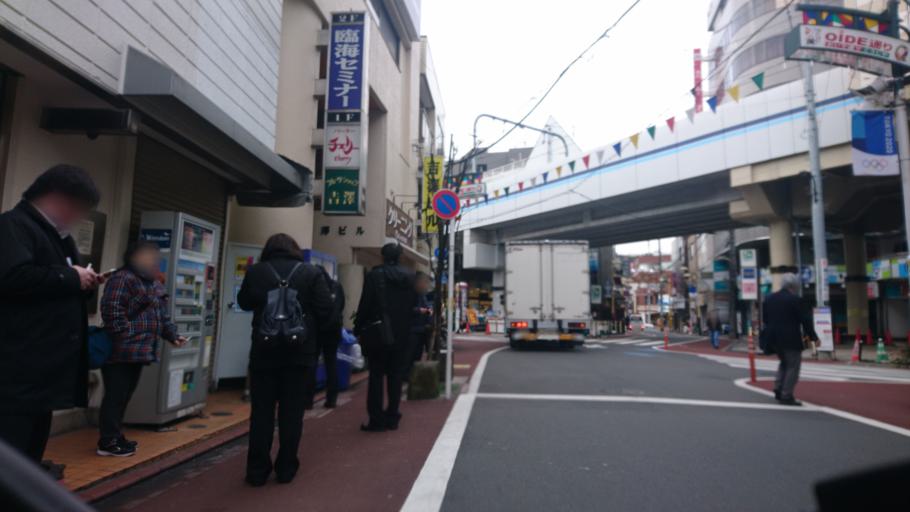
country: JP
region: Kanagawa
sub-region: Kawasaki-shi
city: Kawasaki
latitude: 35.5545
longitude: 139.7301
